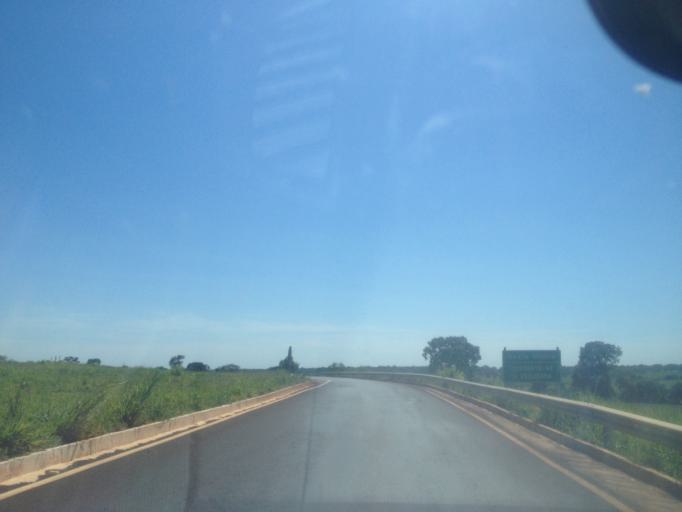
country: BR
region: Minas Gerais
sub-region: Santa Vitoria
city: Santa Vitoria
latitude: -18.8766
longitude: -50.1232
